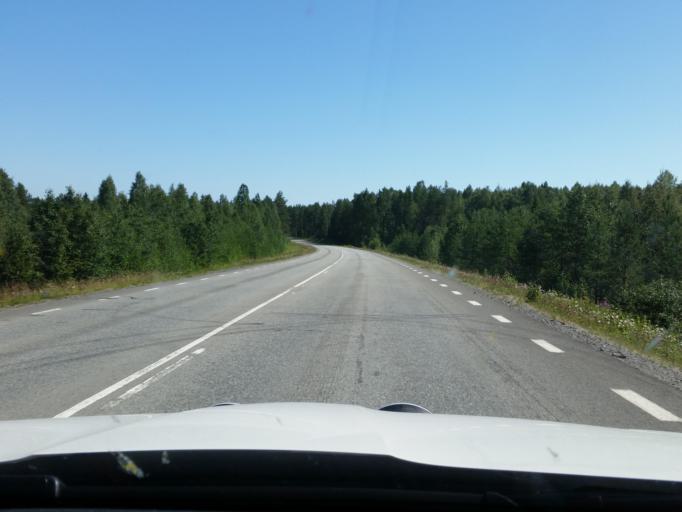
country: SE
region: Norrbotten
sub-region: Alvsbyns Kommun
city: AElvsbyn
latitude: 65.6675
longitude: 20.9679
